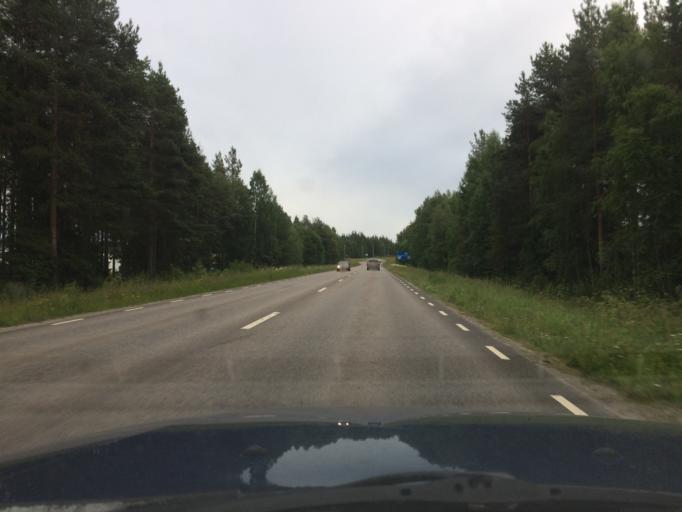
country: SE
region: Norrbotten
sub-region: Pitea Kommun
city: Bergsviken
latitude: 65.3332
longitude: 21.4186
